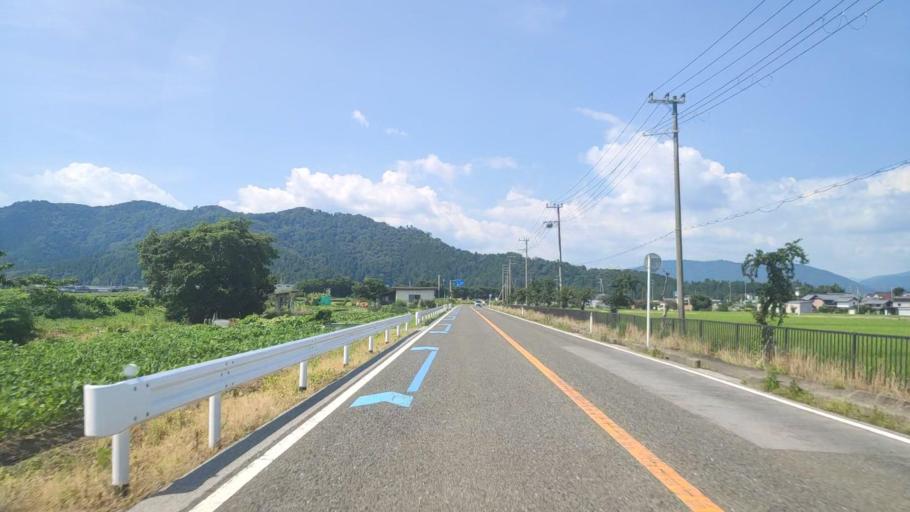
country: JP
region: Shiga Prefecture
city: Nagahama
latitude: 35.4647
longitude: 136.2064
